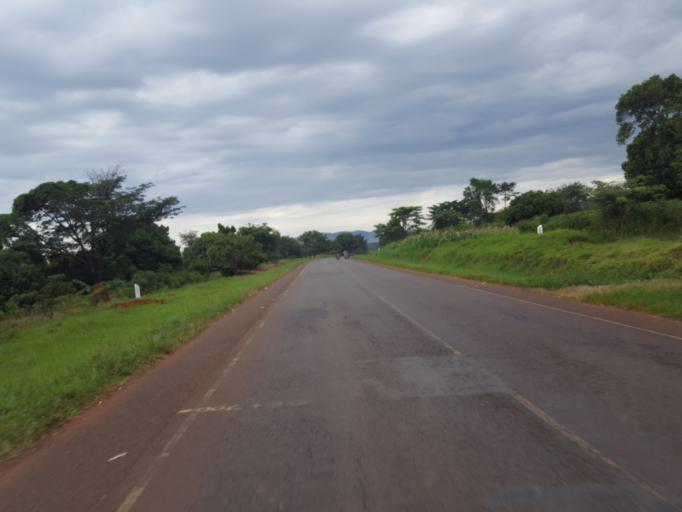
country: UG
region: Central Region
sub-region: Kiboga District
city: Kiboga
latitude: 0.8757
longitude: 31.8493
